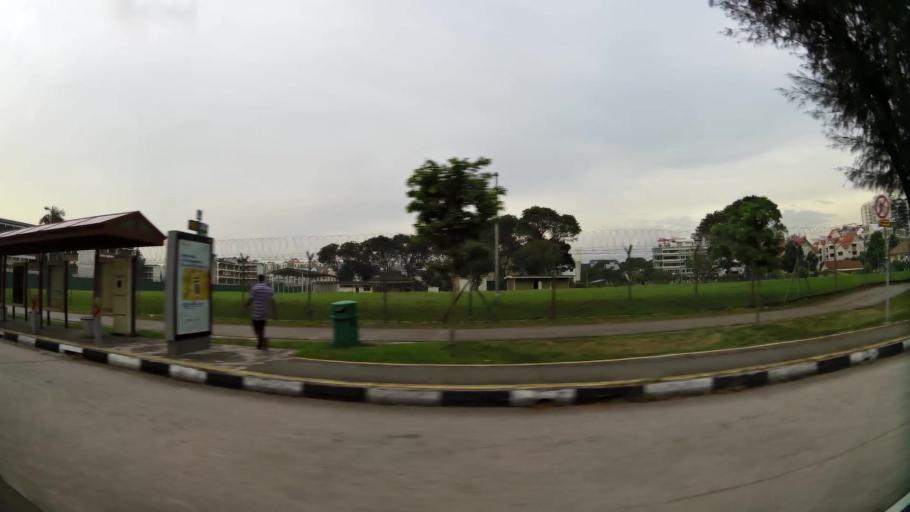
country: SG
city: Singapore
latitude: 1.3091
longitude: 103.8919
